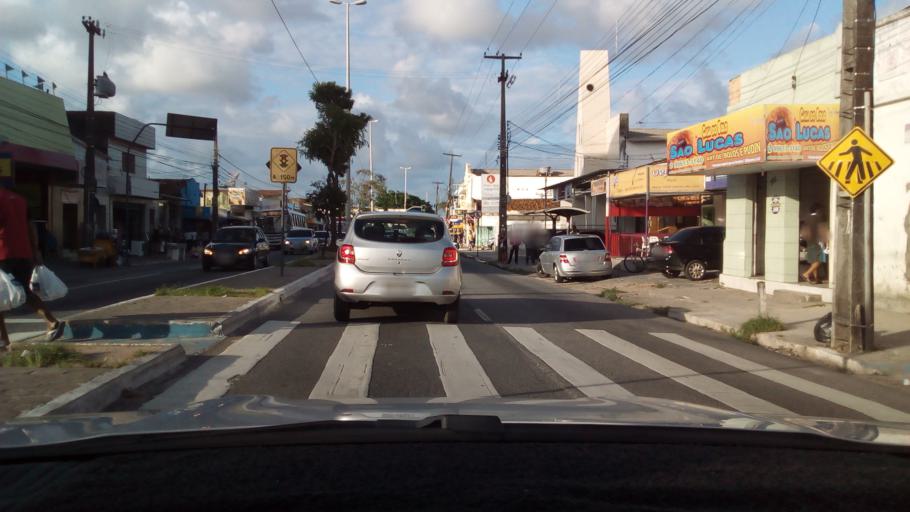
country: BR
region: Paraiba
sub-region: Joao Pessoa
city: Joao Pessoa
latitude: -7.1389
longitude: -34.8884
